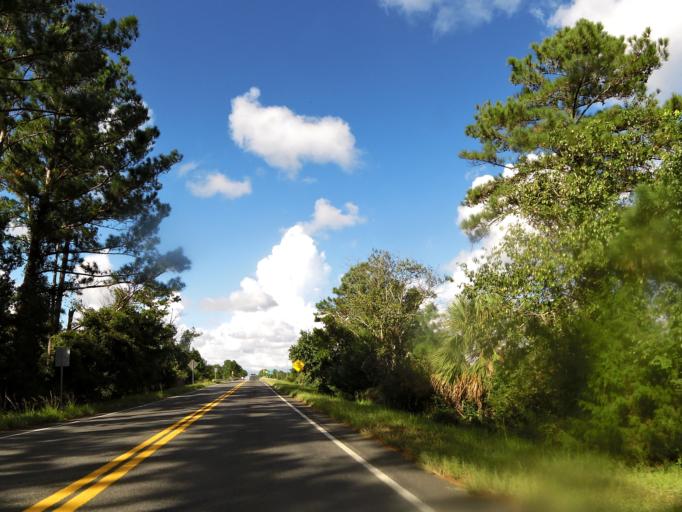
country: US
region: Georgia
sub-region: Glynn County
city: Brunswick
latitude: 31.1123
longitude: -81.6151
